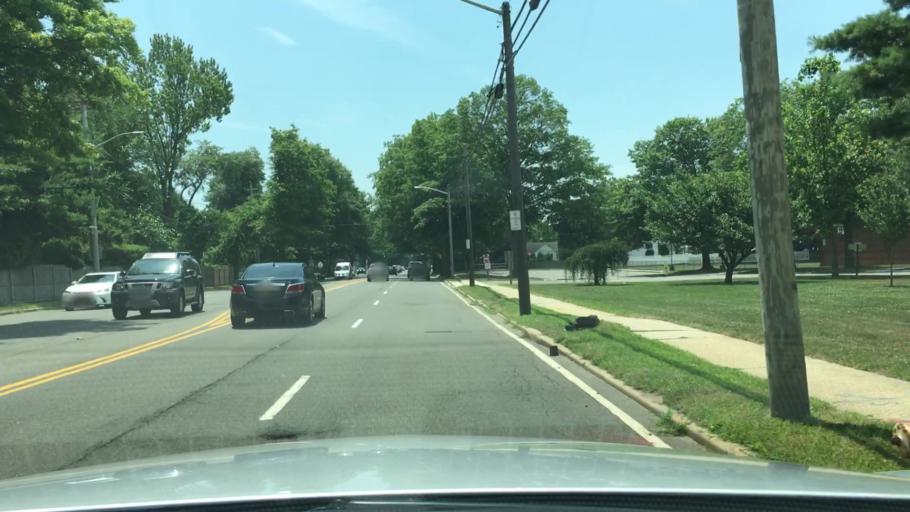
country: US
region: New York
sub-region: Nassau County
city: Plainview
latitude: 40.7930
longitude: -73.4920
